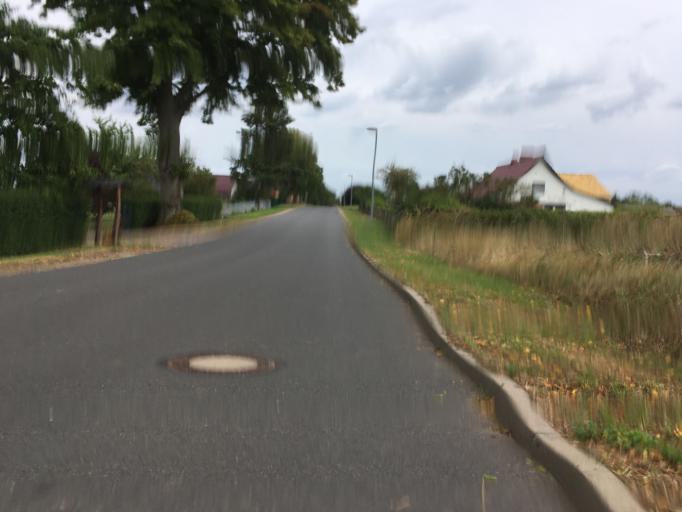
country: DE
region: Brandenburg
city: Zichow
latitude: 53.1895
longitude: 14.0524
